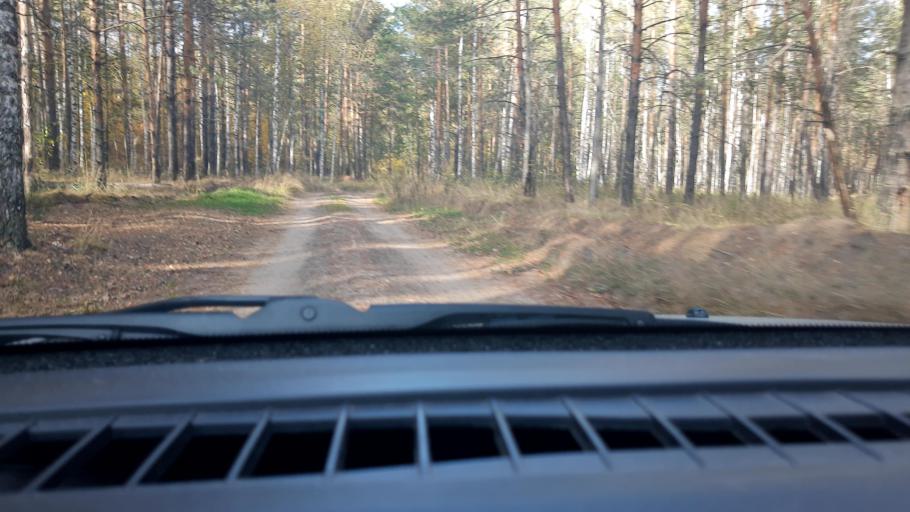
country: RU
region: Nizjnij Novgorod
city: Lukino
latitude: 56.3909
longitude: 43.6281
